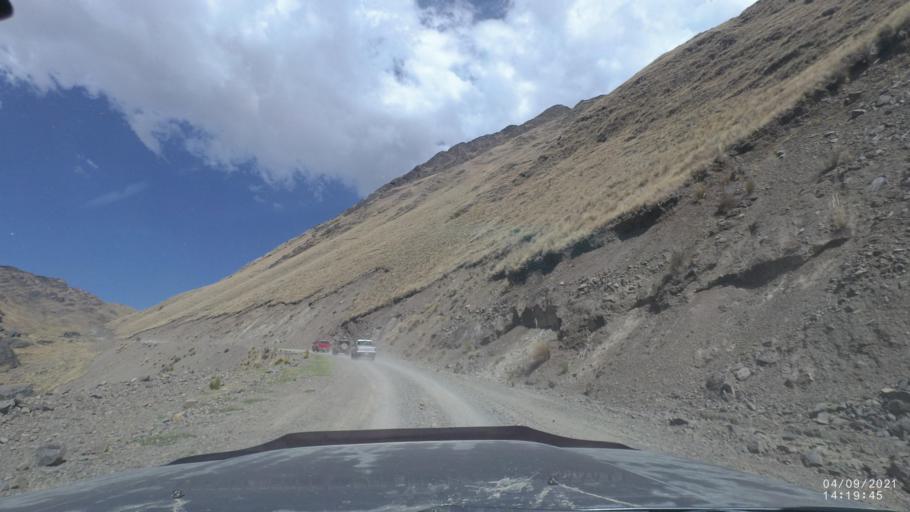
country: BO
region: Cochabamba
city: Sipe Sipe
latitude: -17.2337
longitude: -66.4230
